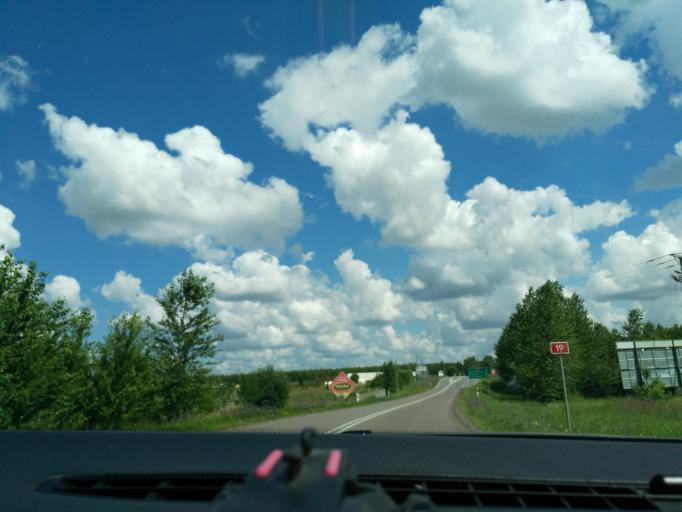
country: PL
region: Podlasie
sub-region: Powiat siemiatycki
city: Siemiatycze
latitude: 52.4420
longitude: 22.8505
